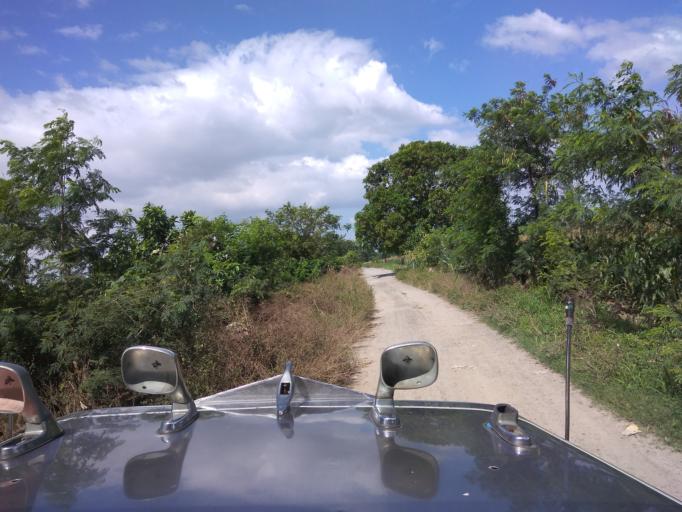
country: PH
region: Central Luzon
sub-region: Province of Pampanga
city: Anao
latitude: 15.1305
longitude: 120.6989
